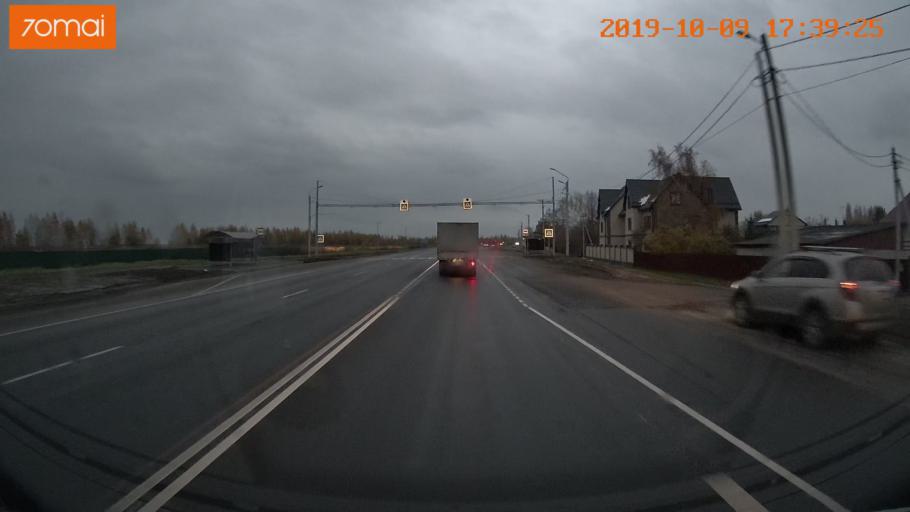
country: RU
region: Ivanovo
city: Bogorodskoye
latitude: 57.0608
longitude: 40.9582
